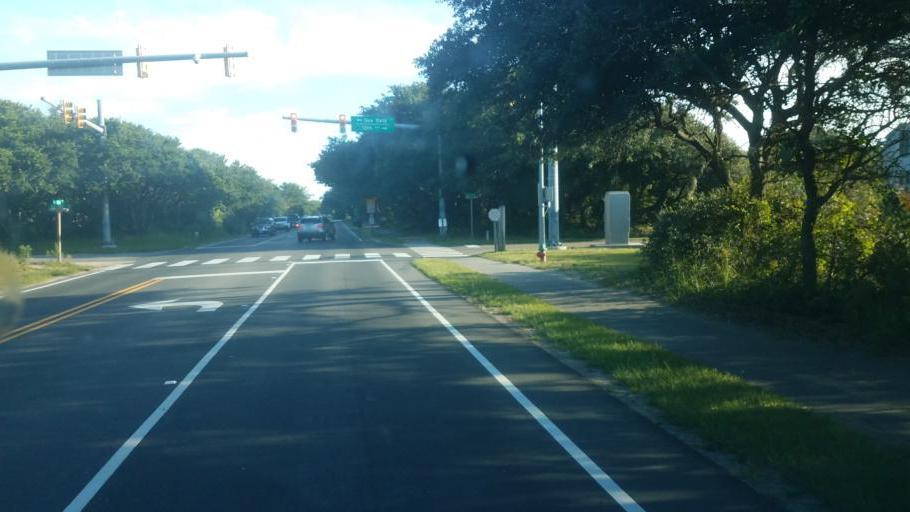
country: US
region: North Carolina
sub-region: Dare County
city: Southern Shores
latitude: 36.1499
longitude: -75.7418
